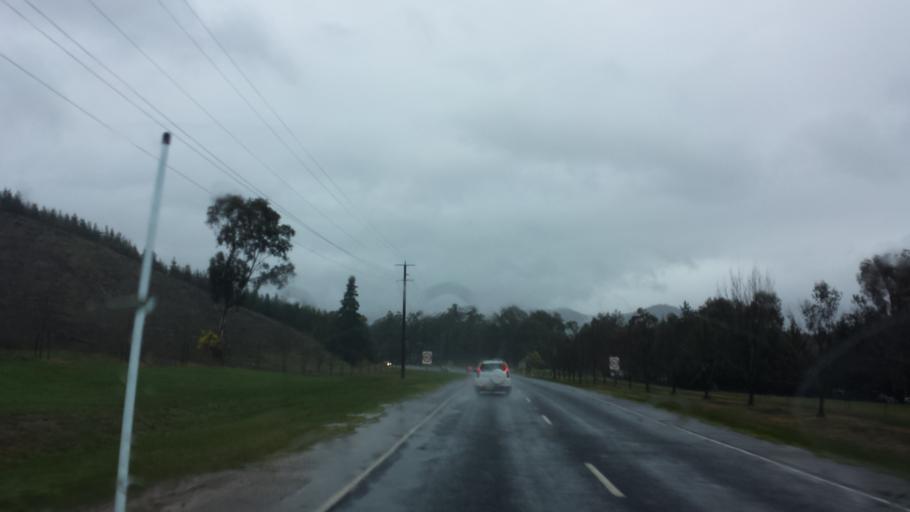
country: AU
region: Victoria
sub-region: Alpine
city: Mount Beauty
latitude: -36.5786
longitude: 146.7498
